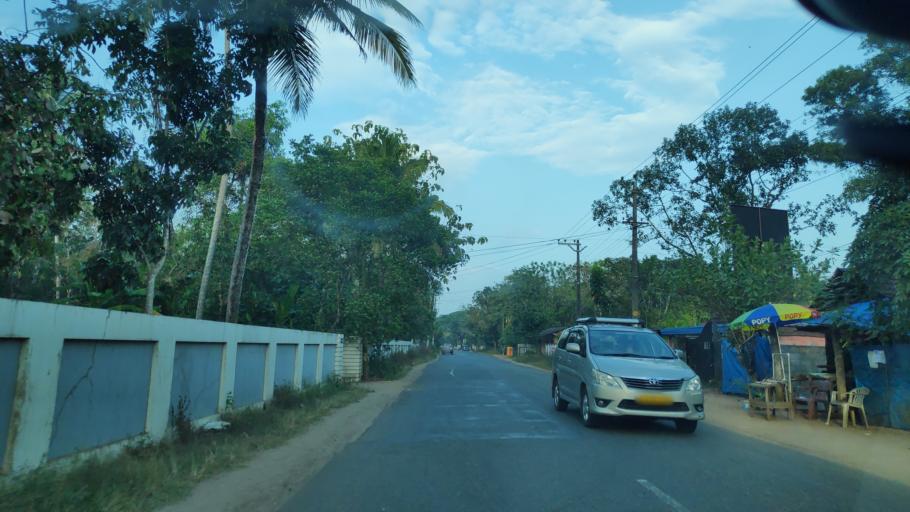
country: IN
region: Kerala
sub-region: Alappuzha
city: Shertallai
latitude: 9.6233
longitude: 76.3655
